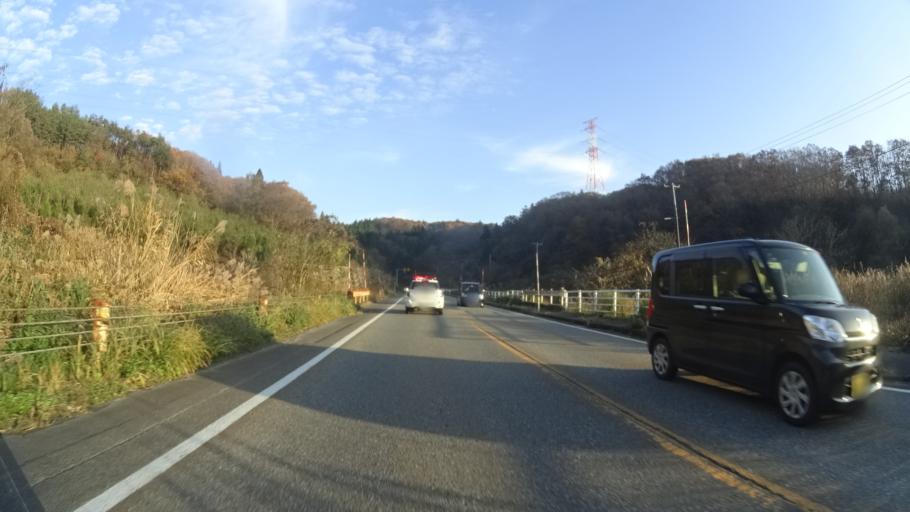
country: JP
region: Niigata
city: Kashiwazaki
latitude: 37.4060
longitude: 138.6884
